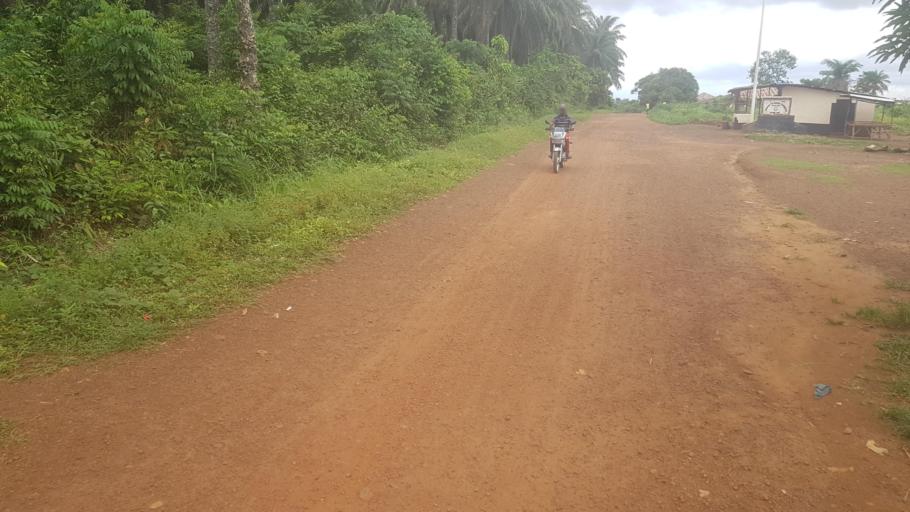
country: SL
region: Southern Province
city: Mogbwemo
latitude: 7.5976
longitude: -12.1746
